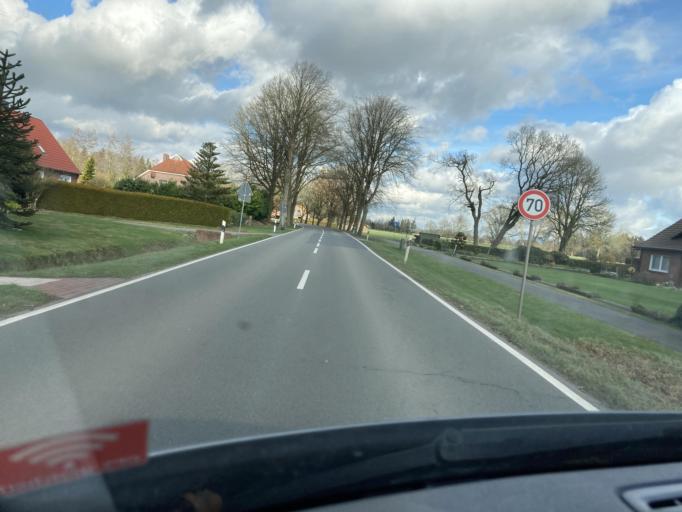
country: DE
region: Lower Saxony
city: Friedeburg
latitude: 53.3571
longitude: 7.8135
